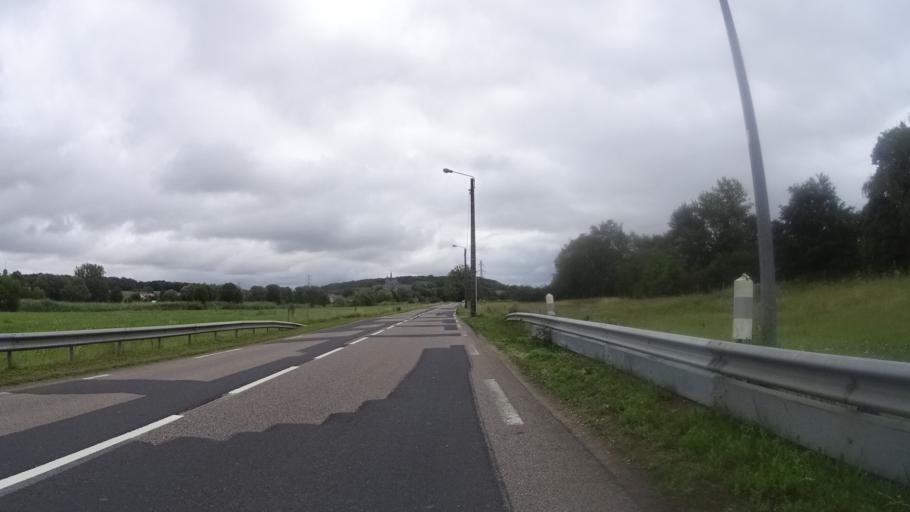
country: FR
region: Lorraine
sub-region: Departement de Meurthe-et-Moselle
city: Laneuveville-devant-Nancy
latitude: 48.6588
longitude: 6.2349
